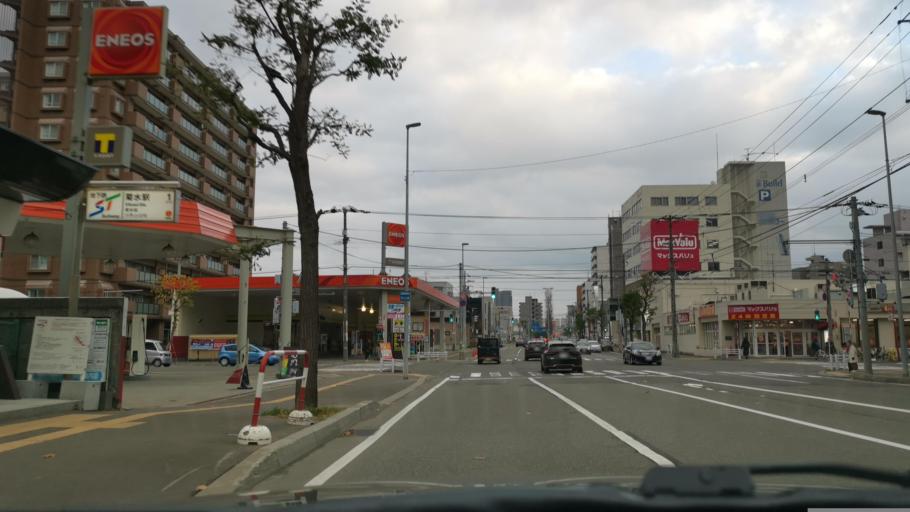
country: JP
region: Hokkaido
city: Sapporo
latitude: 43.0584
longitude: 141.3715
